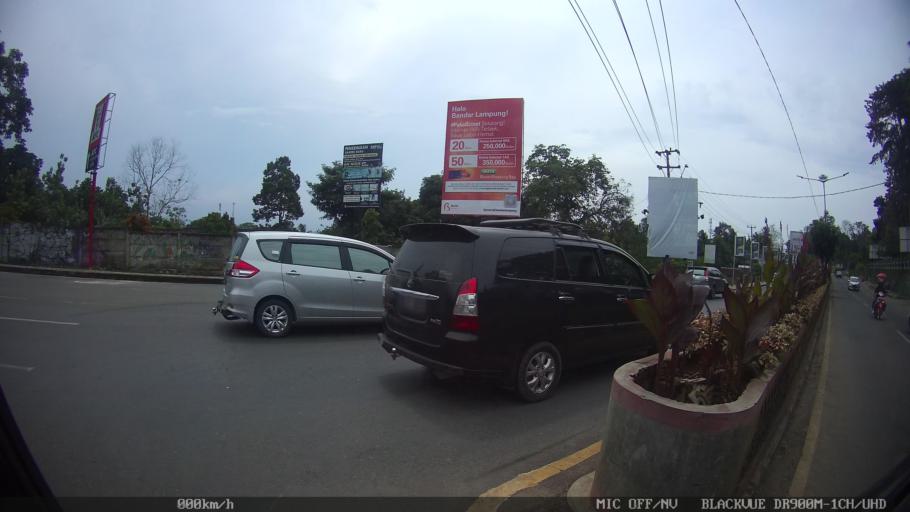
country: ID
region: Lampung
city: Kedaton
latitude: -5.3631
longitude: 105.2266
